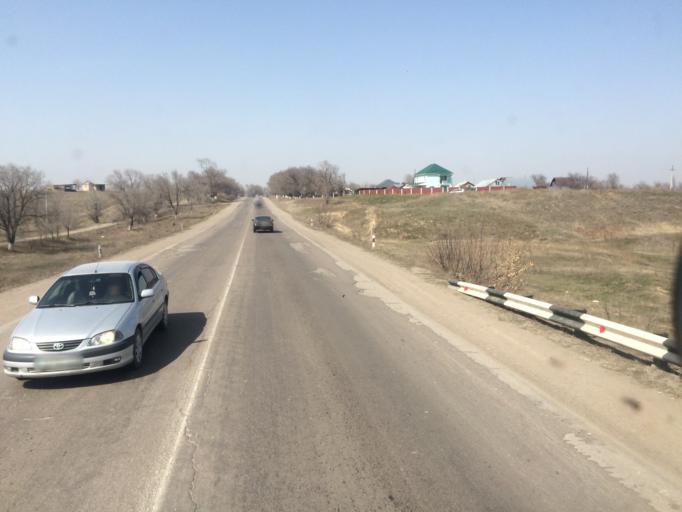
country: KZ
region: Almaty Oblysy
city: Burunday
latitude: 43.3049
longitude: 76.6705
